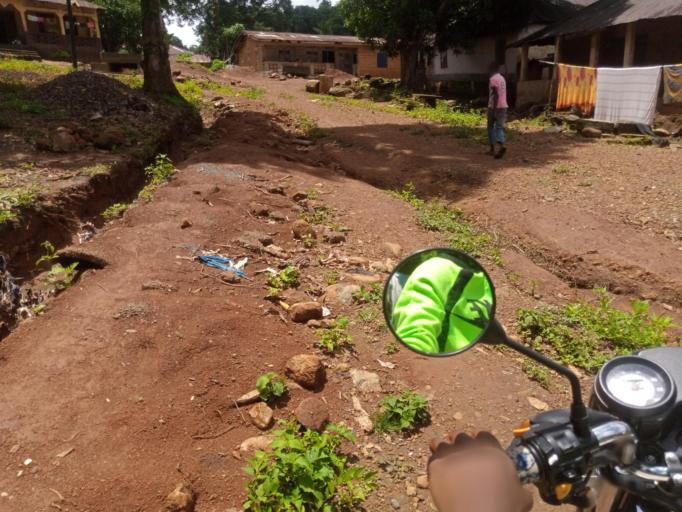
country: SL
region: Northern Province
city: Port Loko
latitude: 8.7624
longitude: -12.7910
